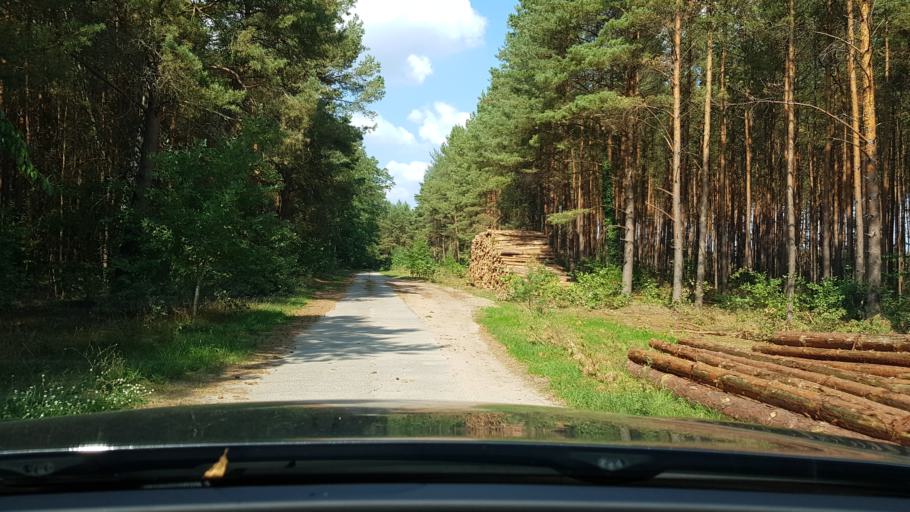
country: DE
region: Brandenburg
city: Rheinsberg
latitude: 53.0617
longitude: 12.9500
